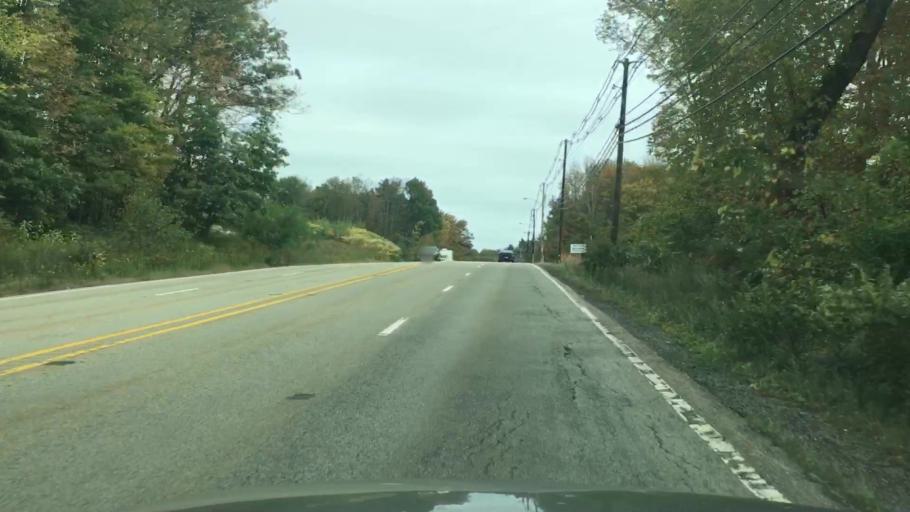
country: US
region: Massachusetts
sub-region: Worcester County
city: Sturbridge
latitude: 42.1361
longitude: -72.0342
